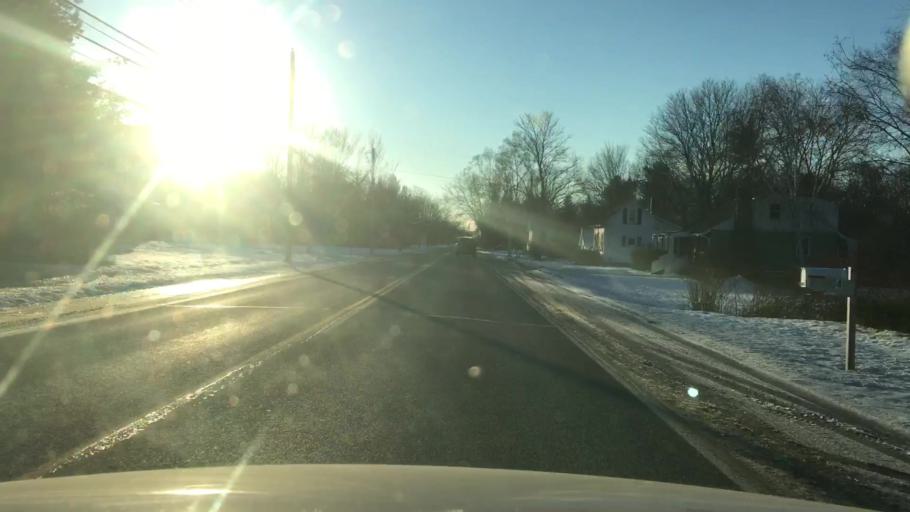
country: US
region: Maine
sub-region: Penobscot County
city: Veazie
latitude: 44.8189
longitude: -68.7189
